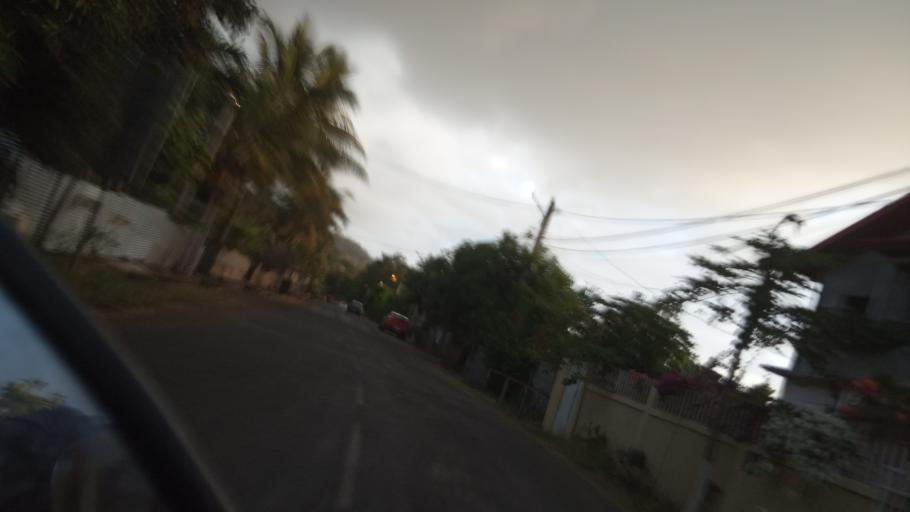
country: YT
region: Kani-Keli
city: Kani Keli
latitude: -12.9279
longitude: 45.1039
